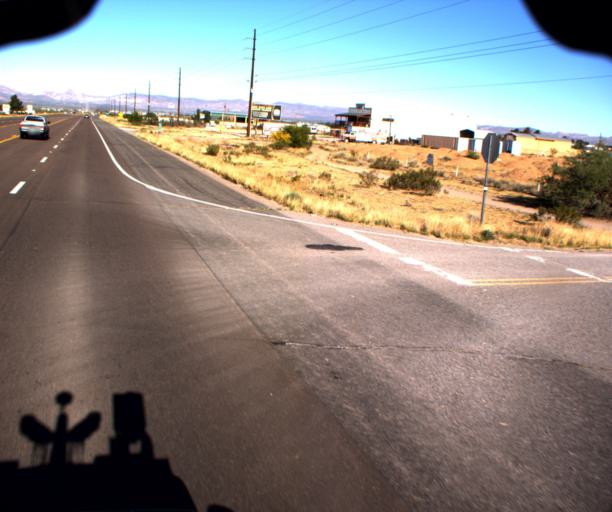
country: US
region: Arizona
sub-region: Mohave County
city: Golden Valley
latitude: 35.2220
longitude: -114.2158
